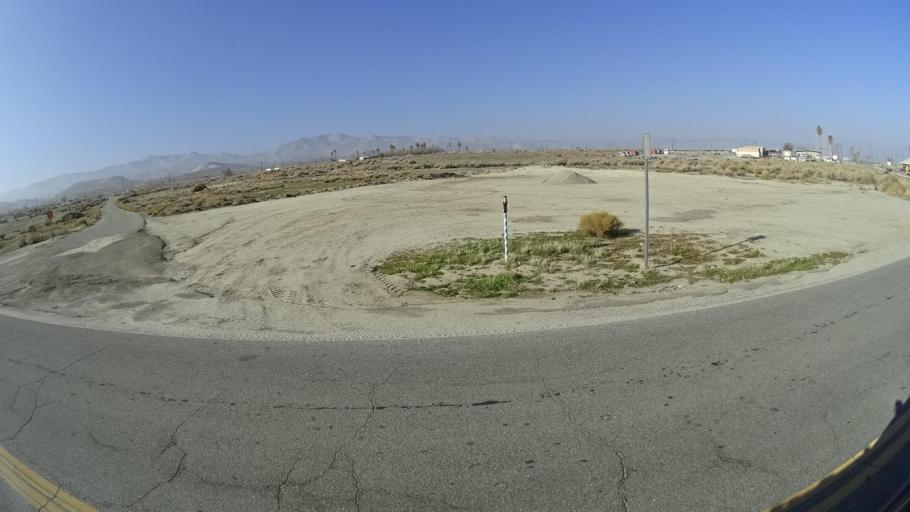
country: US
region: California
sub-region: Kern County
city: Taft Heights
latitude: 35.1837
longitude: -119.5502
